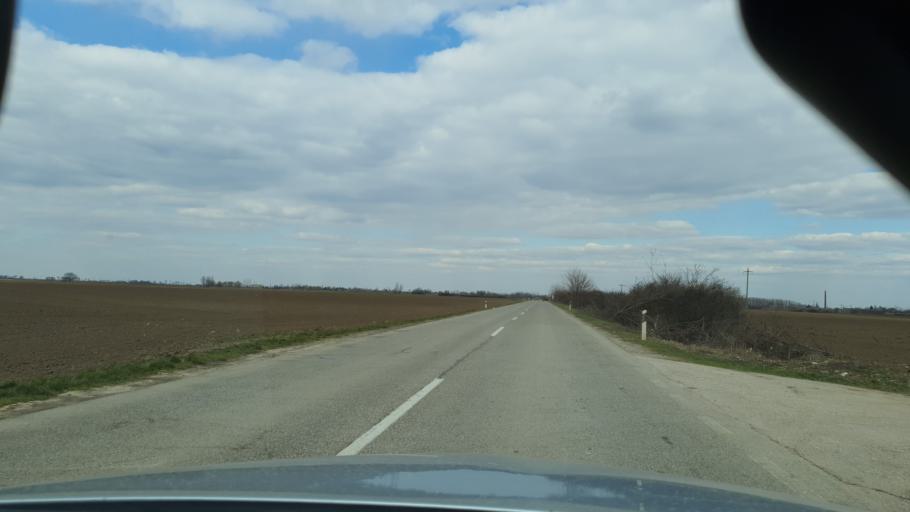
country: RS
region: Autonomna Pokrajina Vojvodina
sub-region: Zapadnobacki Okrug
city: Odzaci
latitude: 45.4386
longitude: 19.3146
